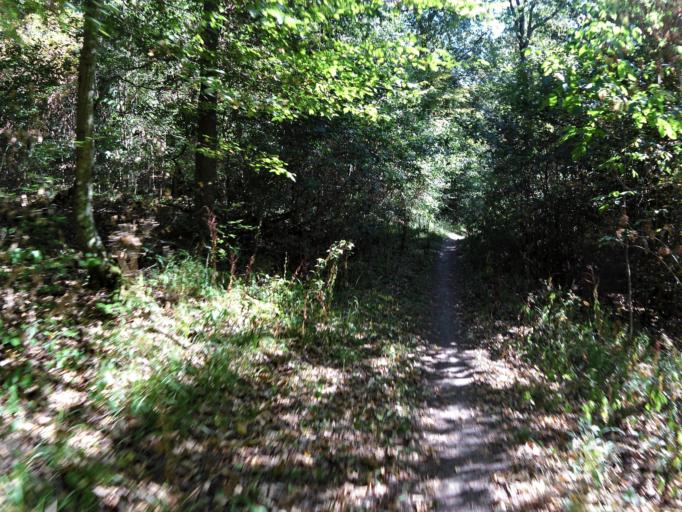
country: DE
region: Bavaria
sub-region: Regierungsbezirk Unterfranken
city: Margetshochheim
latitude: 49.8620
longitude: 9.8694
